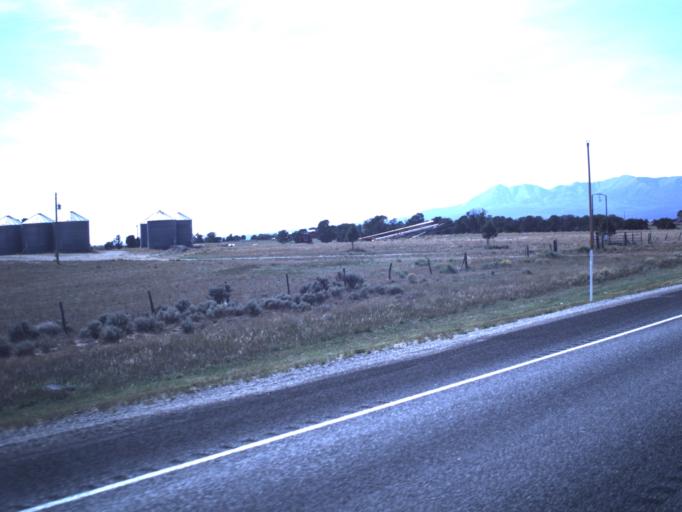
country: US
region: Utah
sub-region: San Juan County
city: Monticello
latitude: 37.8545
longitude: -109.1836
